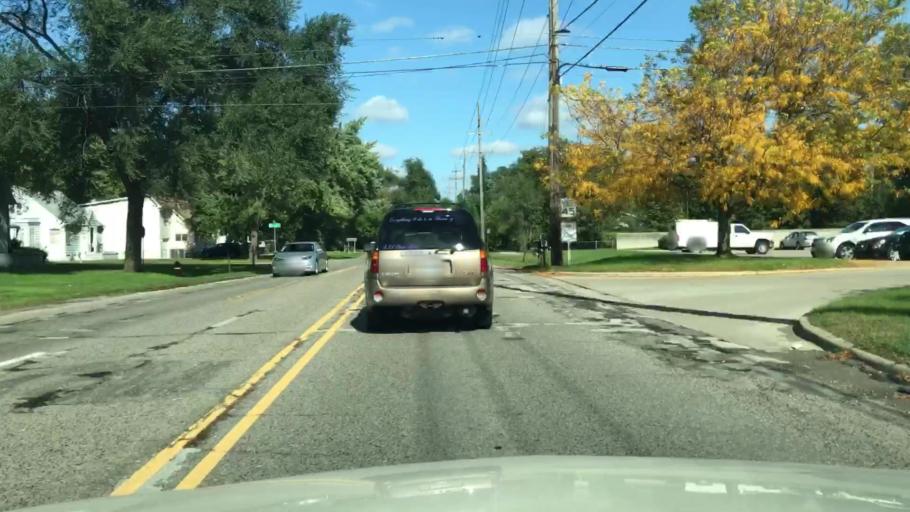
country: US
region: Michigan
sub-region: Oakland County
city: Rochester
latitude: 42.6391
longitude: -83.0921
